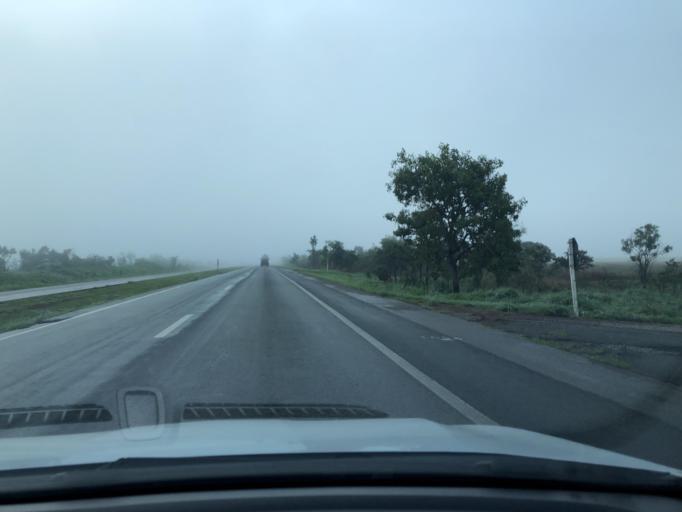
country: BR
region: Goias
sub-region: Luziania
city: Luziania
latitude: -16.2974
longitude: -47.8487
